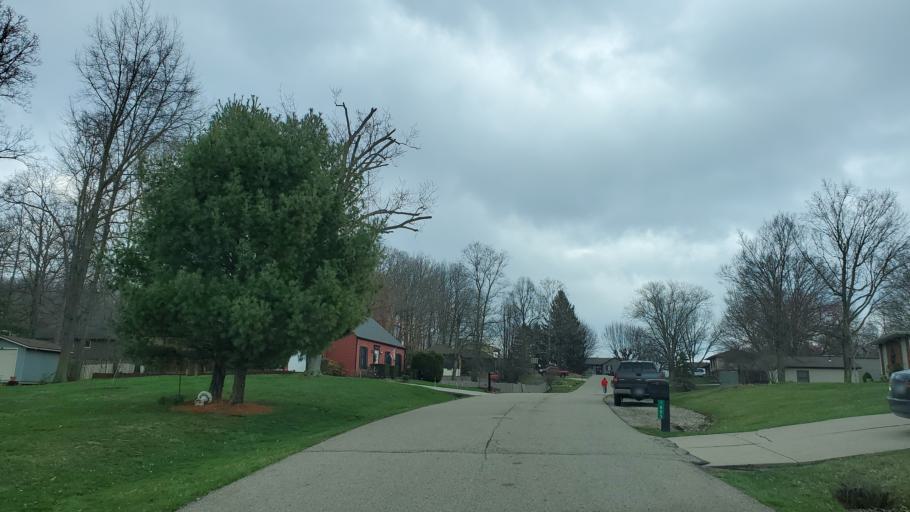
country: US
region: Ohio
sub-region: Licking County
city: Newark
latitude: 40.0214
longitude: -82.3803
